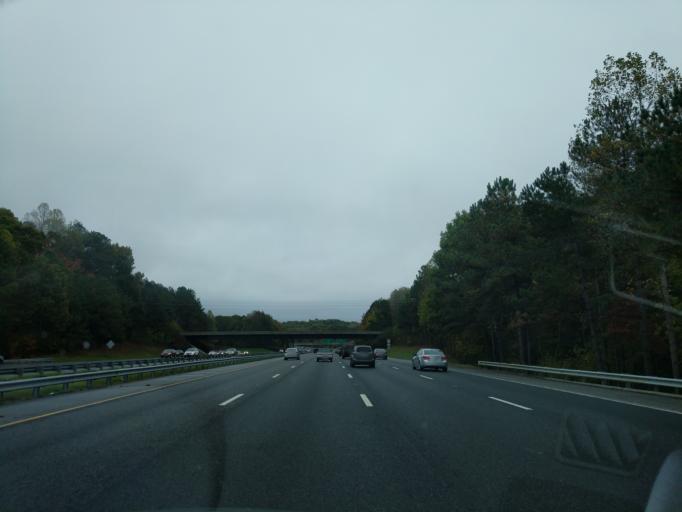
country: US
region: North Carolina
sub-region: Orange County
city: Hillsborough
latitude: 36.0625
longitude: -79.1373
